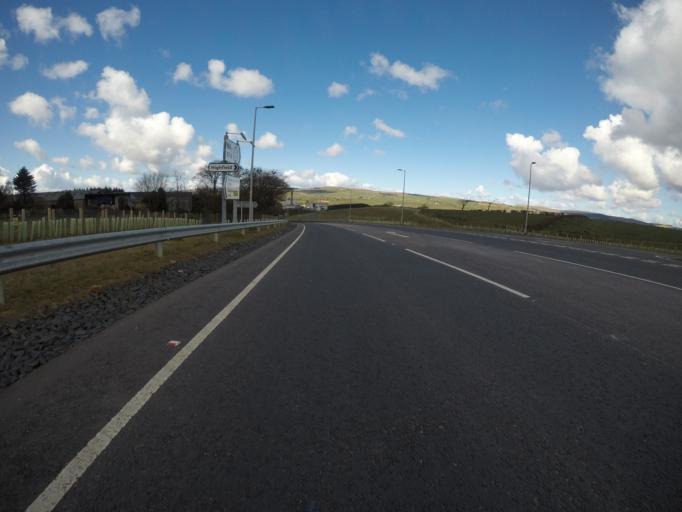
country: GB
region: Scotland
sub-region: North Ayrshire
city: Dalry
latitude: 55.7140
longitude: -4.6956
